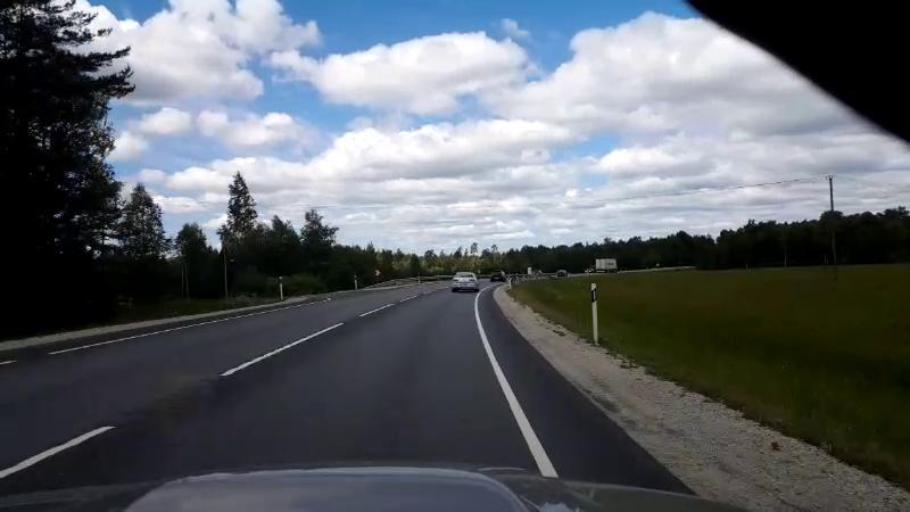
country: EE
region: Paernumaa
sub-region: Halinga vald
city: Parnu-Jaagupi
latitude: 58.6773
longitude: 24.4425
